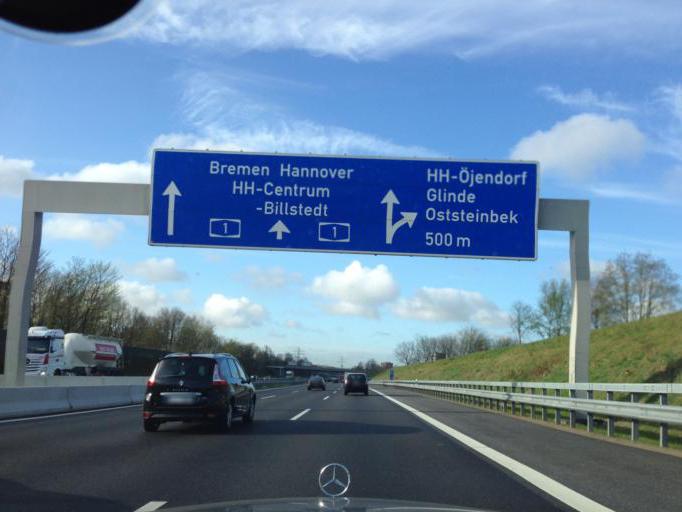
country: DE
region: Schleswig-Holstein
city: Oststeinbek
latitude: 53.5518
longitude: 10.1501
